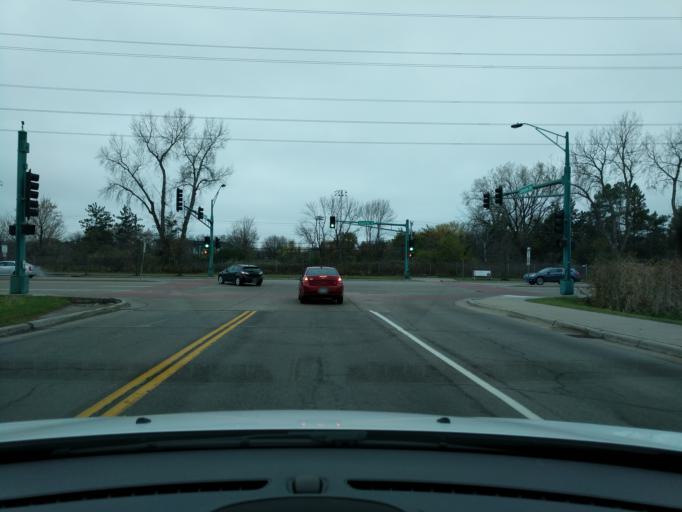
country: US
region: Minnesota
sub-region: Ramsey County
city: Roseville
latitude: 45.0215
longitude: -93.1688
